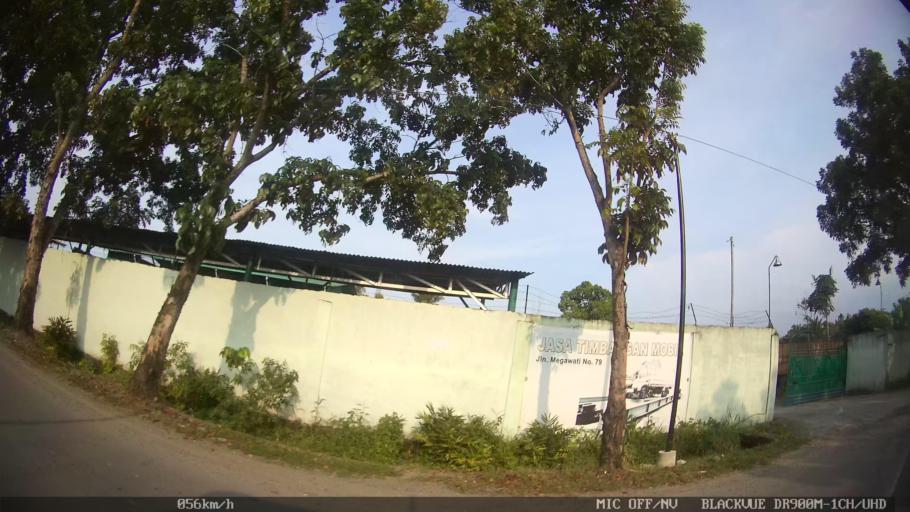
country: ID
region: North Sumatra
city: Binjai
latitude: 3.6169
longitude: 98.5346
